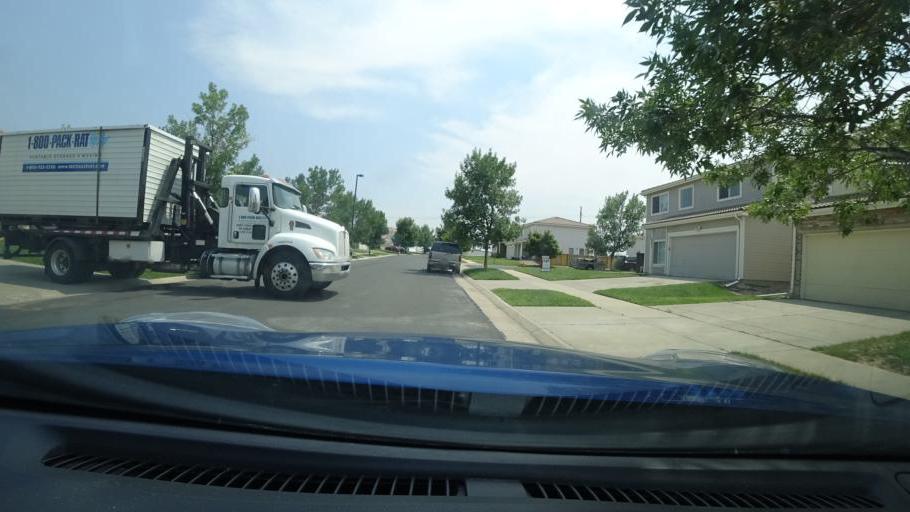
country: US
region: Colorado
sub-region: Adams County
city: Aurora
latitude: 39.7704
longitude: -104.7410
